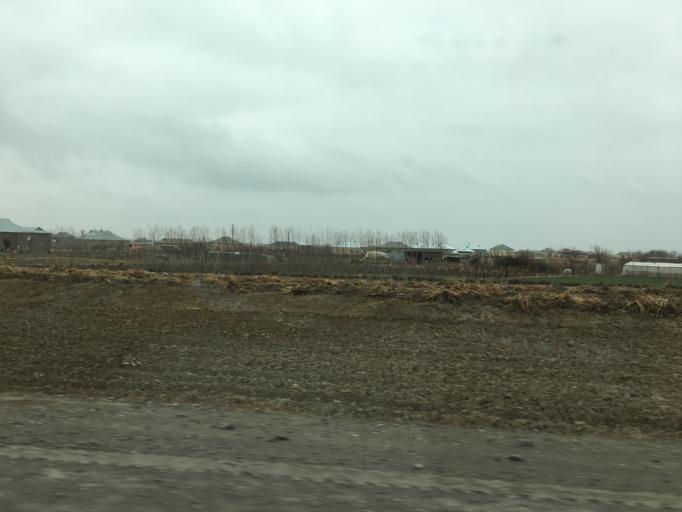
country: TM
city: Murgab
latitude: 37.4715
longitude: 62.0264
